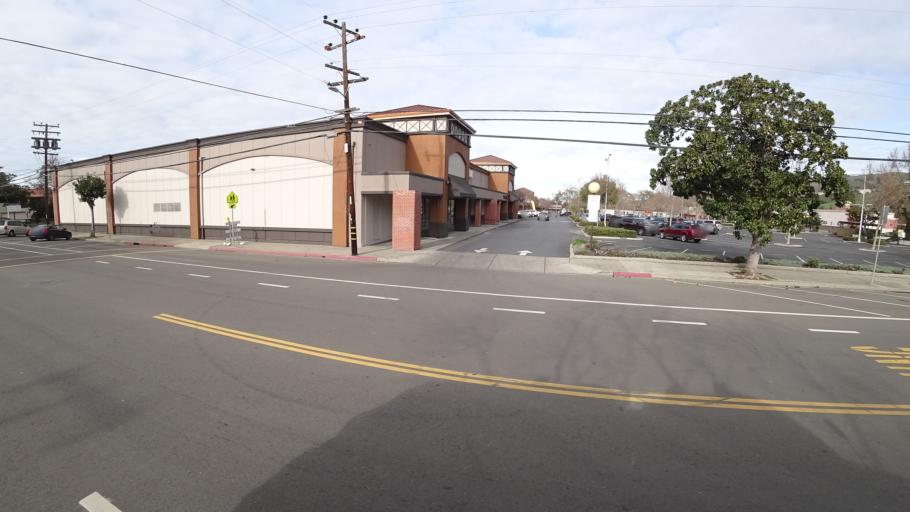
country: US
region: California
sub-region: Alameda County
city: Union City
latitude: 37.6180
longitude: -122.0352
